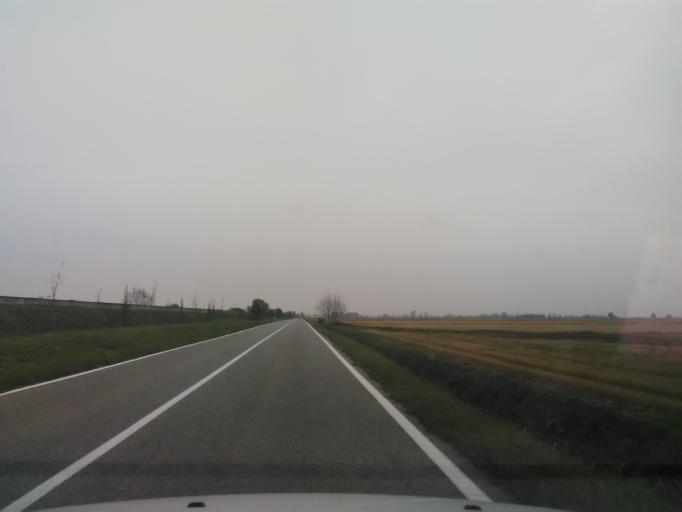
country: IT
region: Piedmont
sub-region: Provincia di Vercelli
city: Bianze
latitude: 45.2641
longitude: 8.1449
